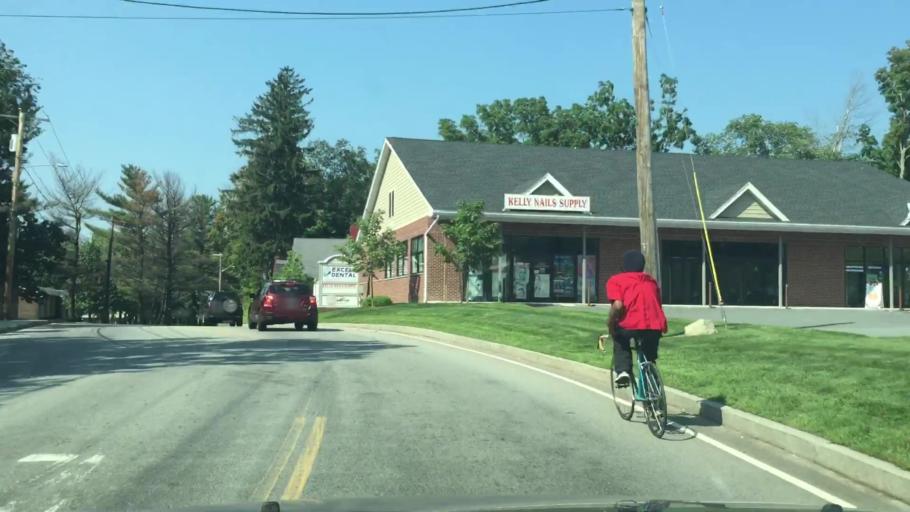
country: US
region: Massachusetts
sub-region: Middlesex County
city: Chelmsford
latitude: 42.6300
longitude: -71.3549
